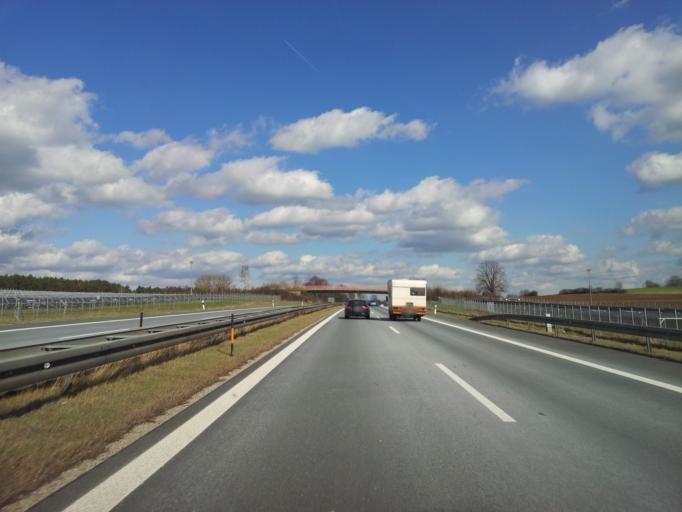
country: DE
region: Bavaria
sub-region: Upper Franconia
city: Kasendorf
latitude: 50.0085
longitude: 11.3444
